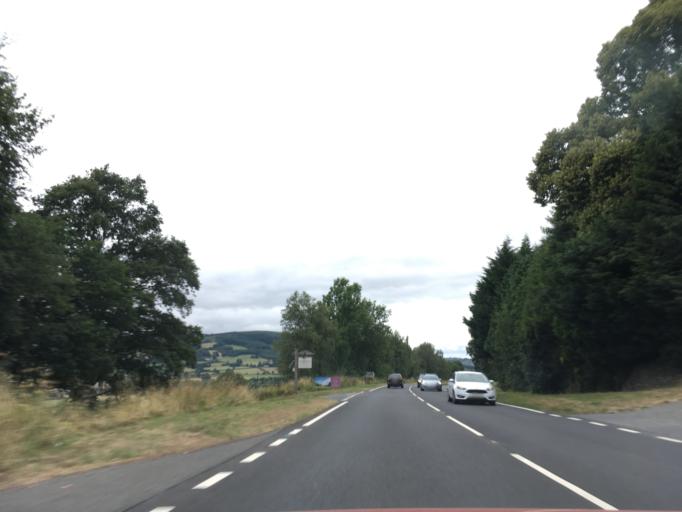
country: GB
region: Wales
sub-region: Blaenau Gwent
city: Tredegar
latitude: 51.8946
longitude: -3.2633
